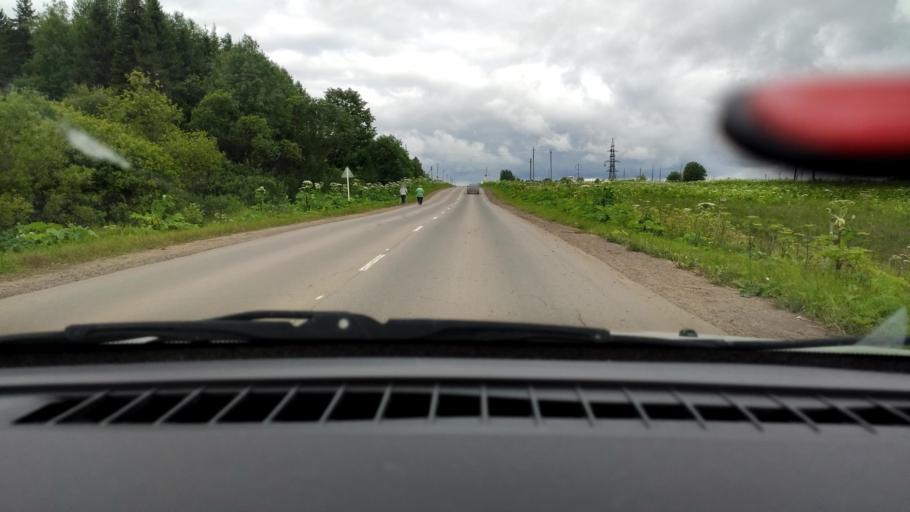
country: RU
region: Perm
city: Chaykovskaya
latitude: 58.1223
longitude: 55.5606
